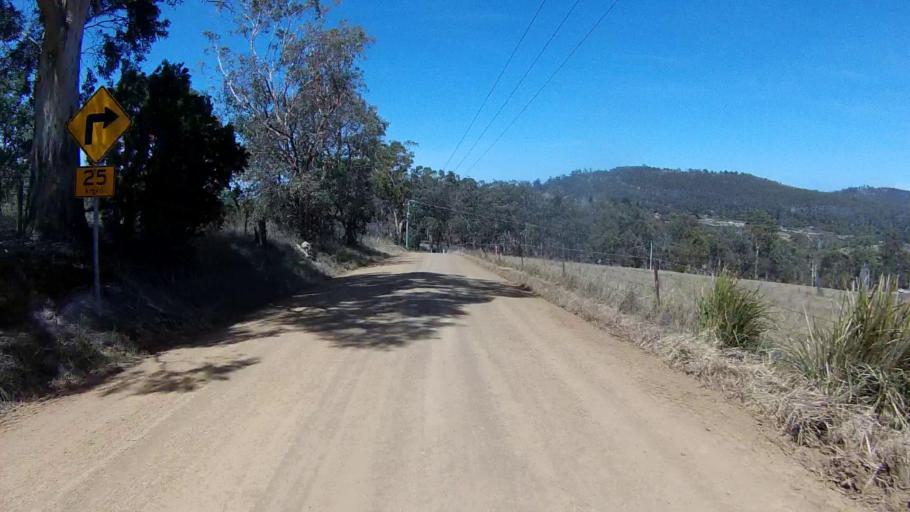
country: AU
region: Tasmania
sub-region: Sorell
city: Sorell
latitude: -42.7824
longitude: 147.6440
